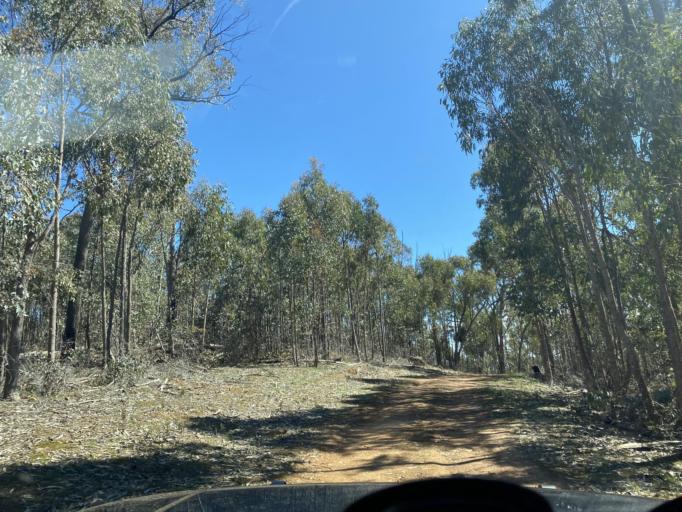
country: AU
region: Victoria
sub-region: Benalla
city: Benalla
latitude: -36.7251
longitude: 146.1809
